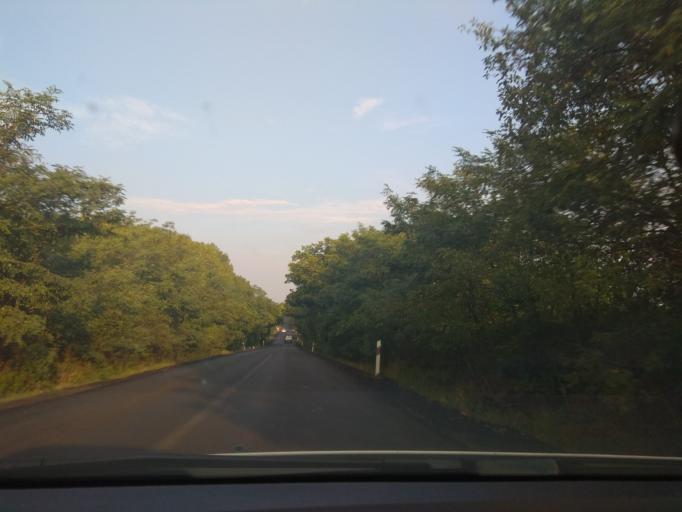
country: HU
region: Heves
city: Szihalom
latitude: 47.8187
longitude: 20.5050
